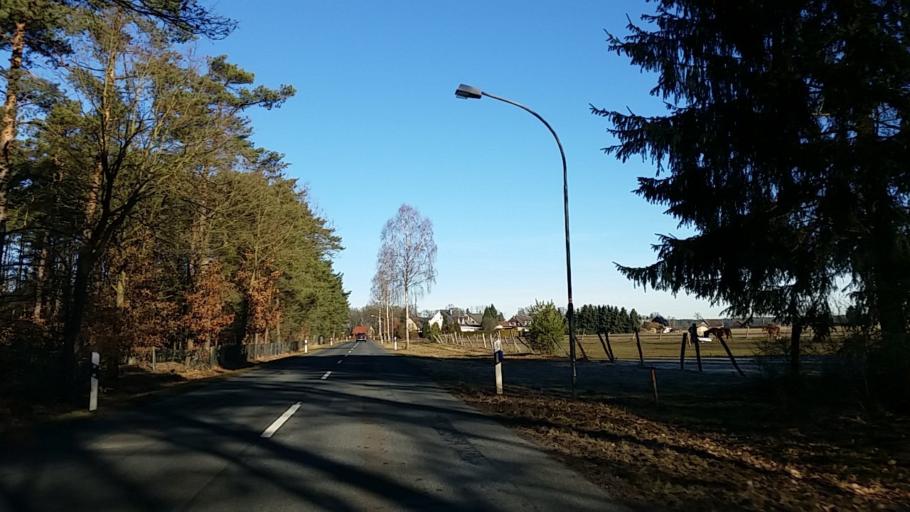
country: DE
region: Lower Saxony
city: Sassenburg
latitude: 52.5488
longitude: 10.6797
